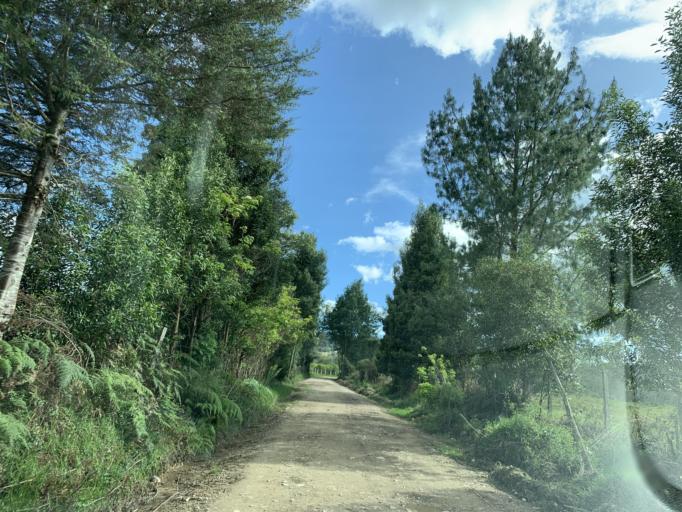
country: CO
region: Boyaca
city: Arcabuco
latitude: 5.7859
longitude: -73.4597
